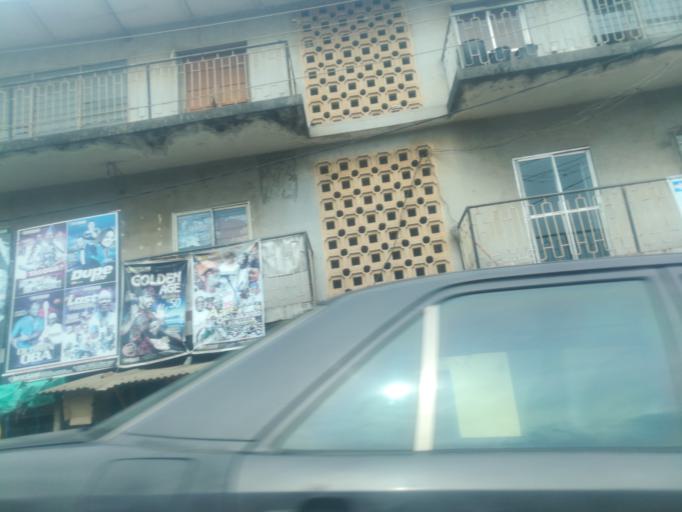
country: NG
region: Oyo
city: Ibadan
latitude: 7.4123
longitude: 3.8929
